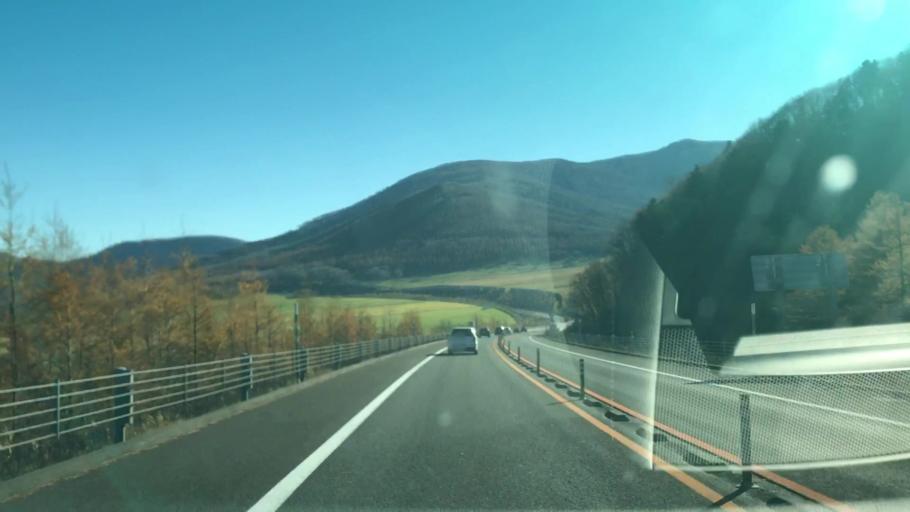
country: JP
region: Hokkaido
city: Otofuke
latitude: 43.0497
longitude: 142.7846
